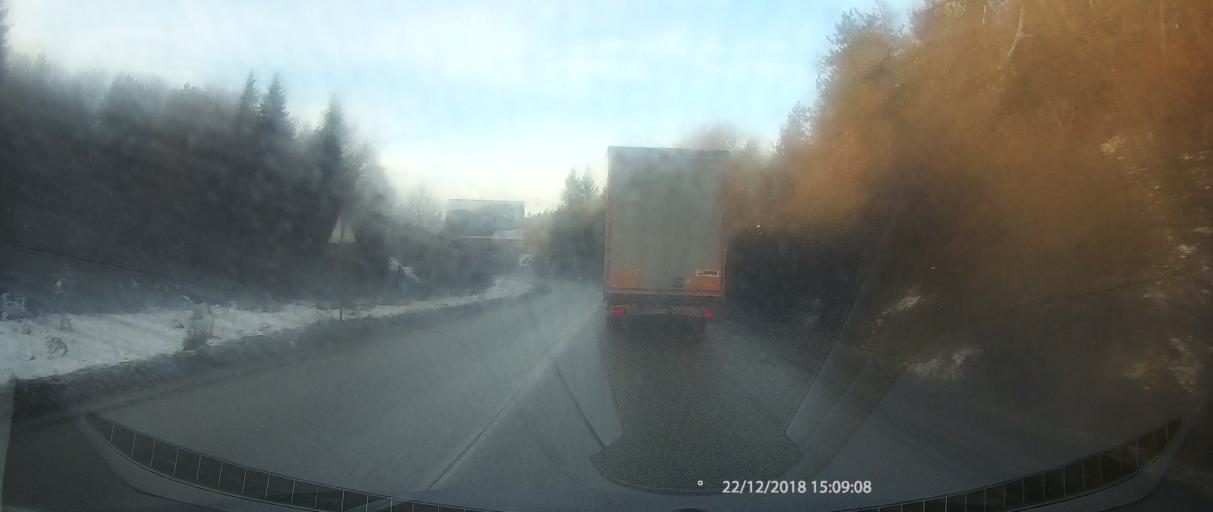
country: BG
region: Ruse
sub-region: Obshtina Borovo
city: Borovo
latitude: 43.5010
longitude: 25.7977
